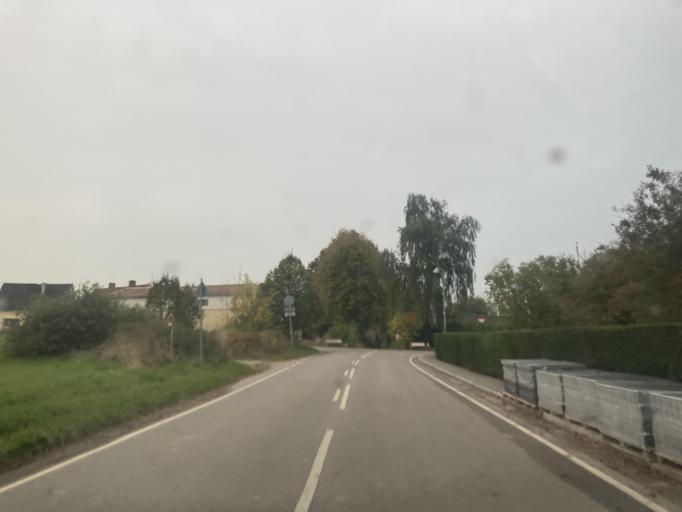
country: DK
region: Capital Region
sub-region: Egedal Kommune
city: Vekso
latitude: 55.7138
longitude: 12.2163
